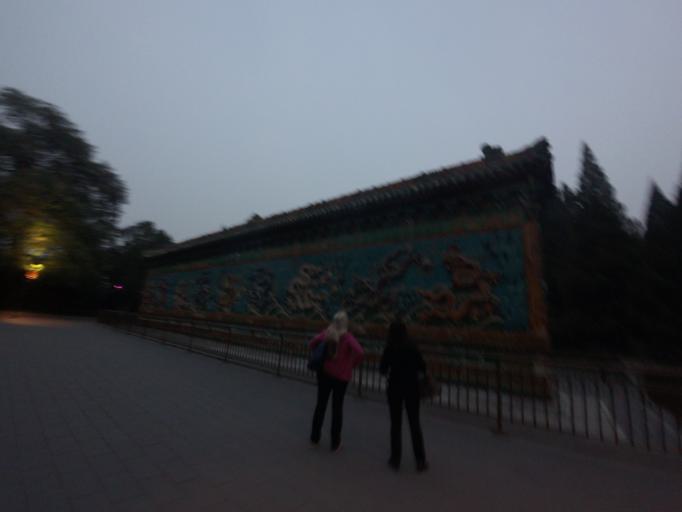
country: CN
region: Beijing
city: Jingshan
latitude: 39.9305
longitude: 116.3813
